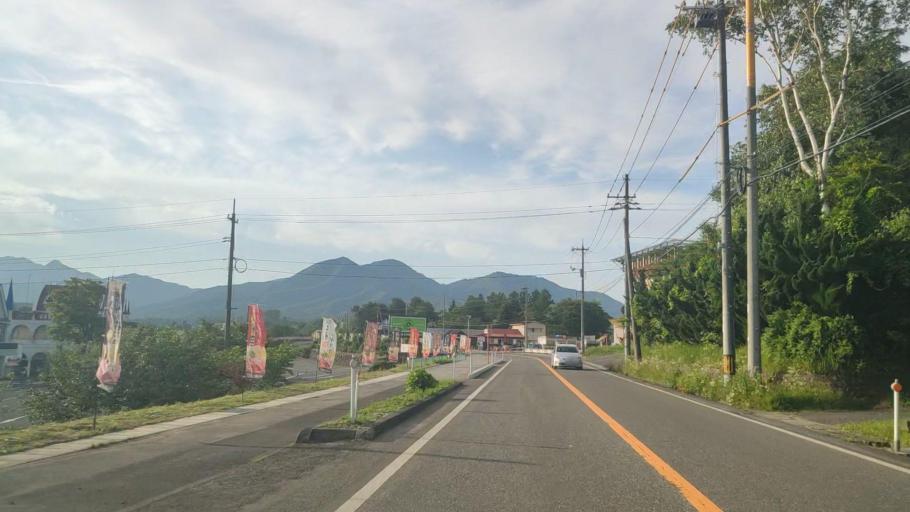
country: JP
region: Tottori
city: Kurayoshi
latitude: 35.2901
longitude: 133.6366
